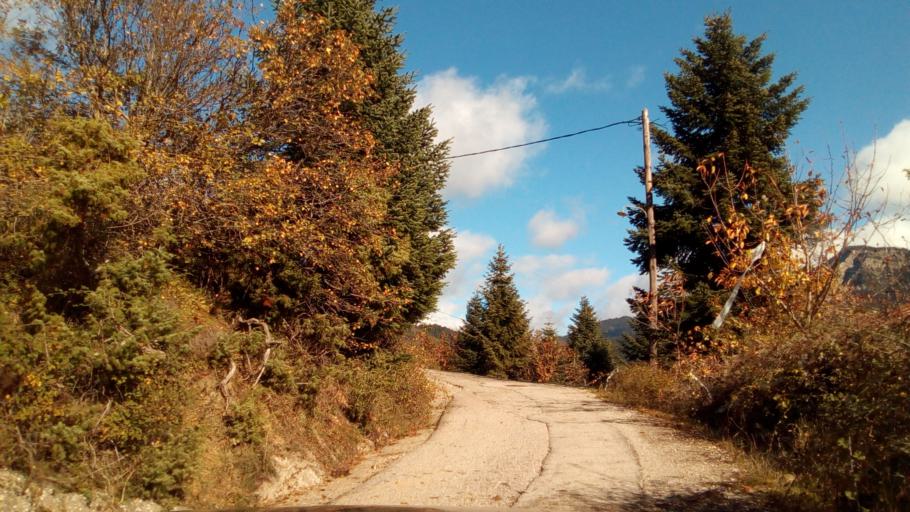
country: GR
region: West Greece
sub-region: Nomos Aitolias kai Akarnanias
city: Nafpaktos
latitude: 38.5944
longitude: 21.9264
